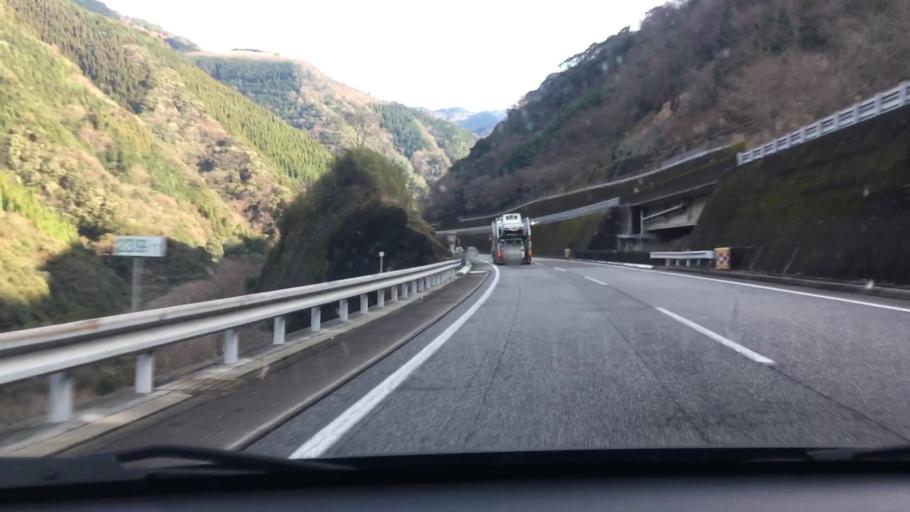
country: JP
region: Kumamoto
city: Hitoyoshi
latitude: 32.3283
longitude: 130.7502
